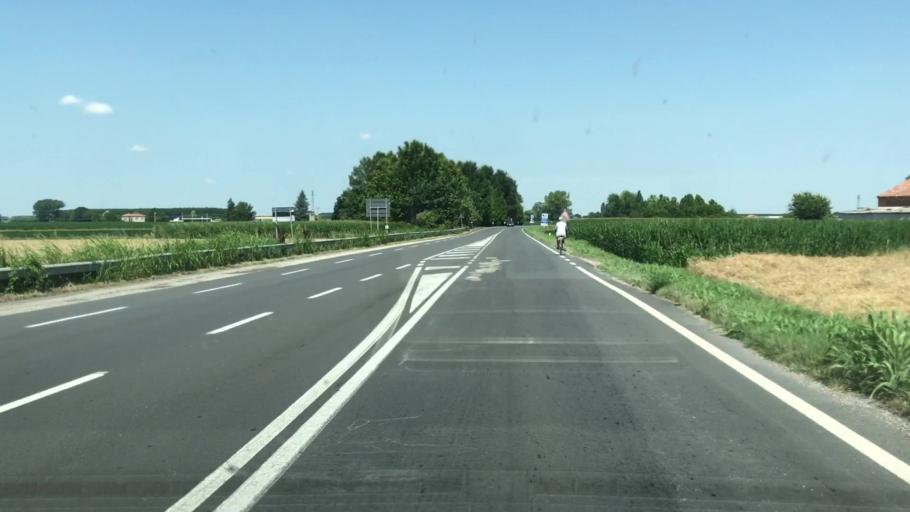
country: IT
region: Veneto
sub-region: Provincia di Rovigo
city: Castelnovo Bariano
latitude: 45.0342
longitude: 11.2980
